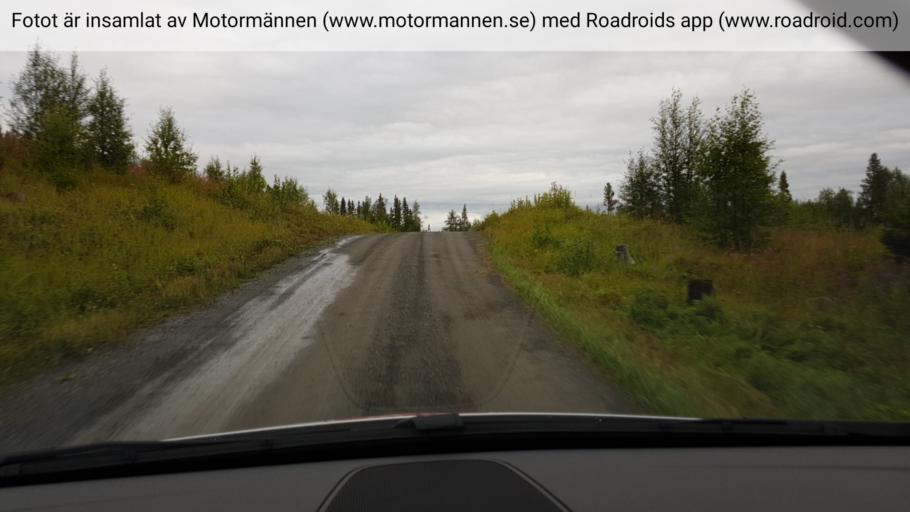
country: SE
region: Jaemtland
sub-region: OEstersunds Kommun
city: Lit
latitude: 63.5492
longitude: 14.7382
